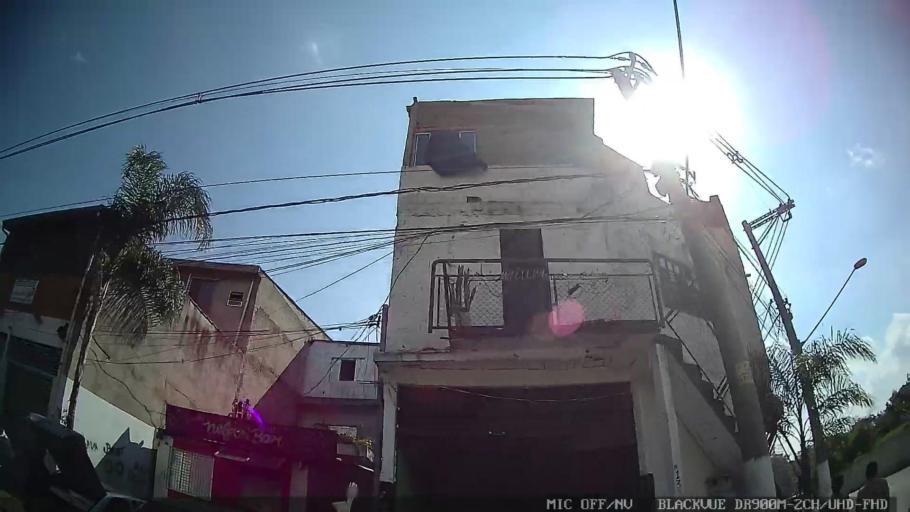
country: BR
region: Sao Paulo
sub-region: Guarulhos
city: Guarulhos
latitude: -23.4835
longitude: -46.4573
